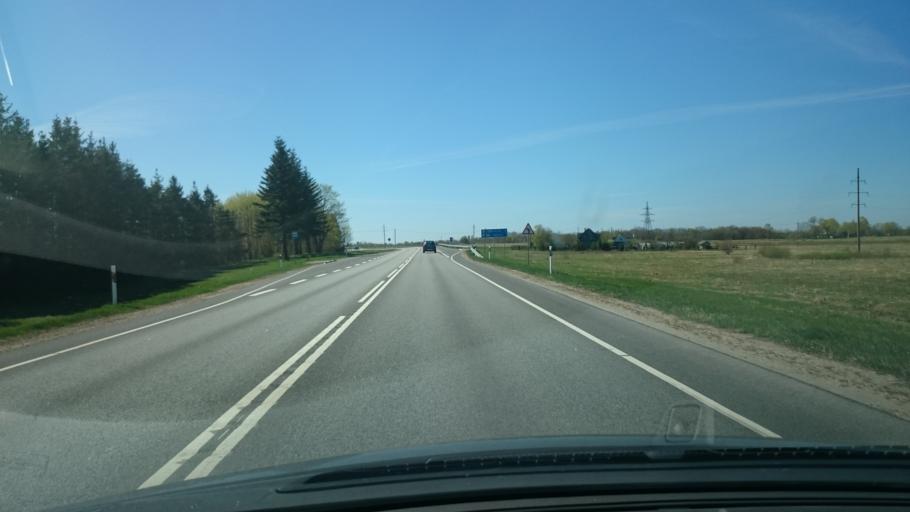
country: EE
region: Ida-Virumaa
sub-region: Narva-Joesuu linn
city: Narva-Joesuu
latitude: 59.4066
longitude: 28.0351
